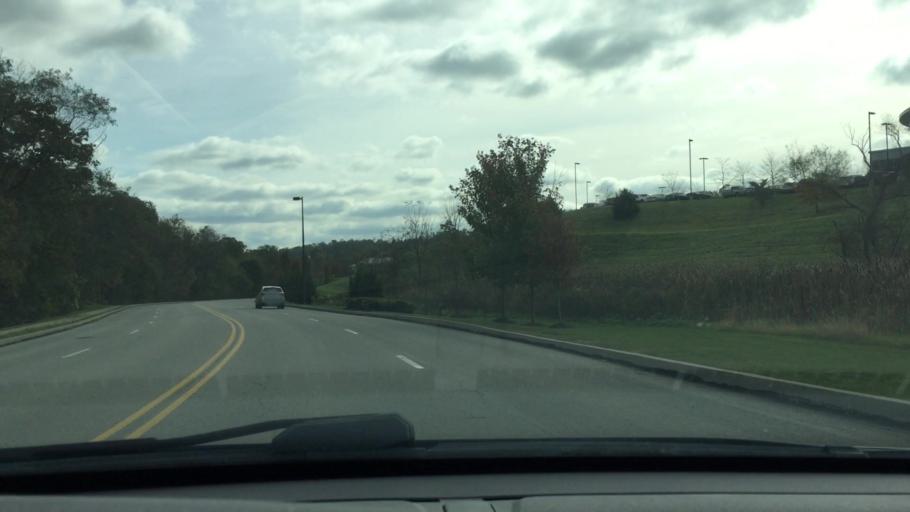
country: US
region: Pennsylvania
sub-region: Washington County
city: Canonsburg
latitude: 40.2810
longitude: -80.1675
